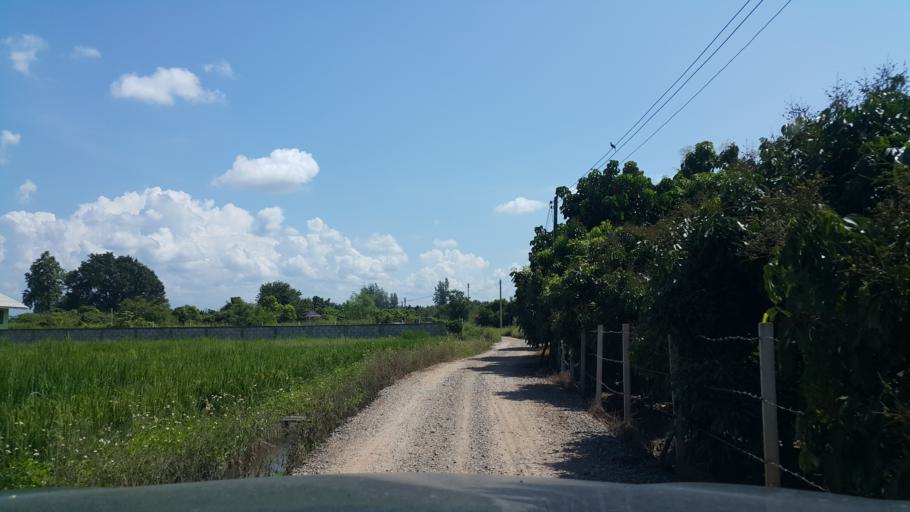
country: TH
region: Chiang Mai
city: Chom Thong
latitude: 18.4184
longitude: 98.6826
